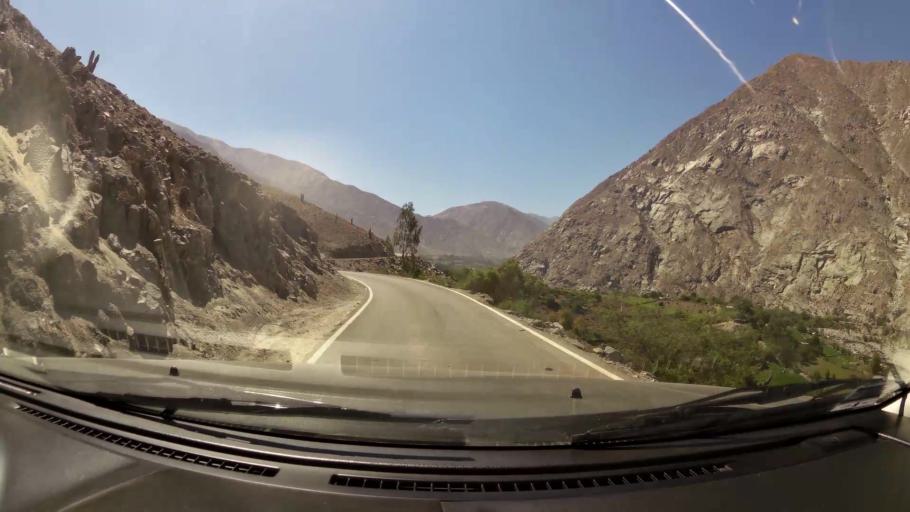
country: PE
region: Ica
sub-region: Provincia de Pisco
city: Huancano
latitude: -13.8296
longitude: -75.5410
